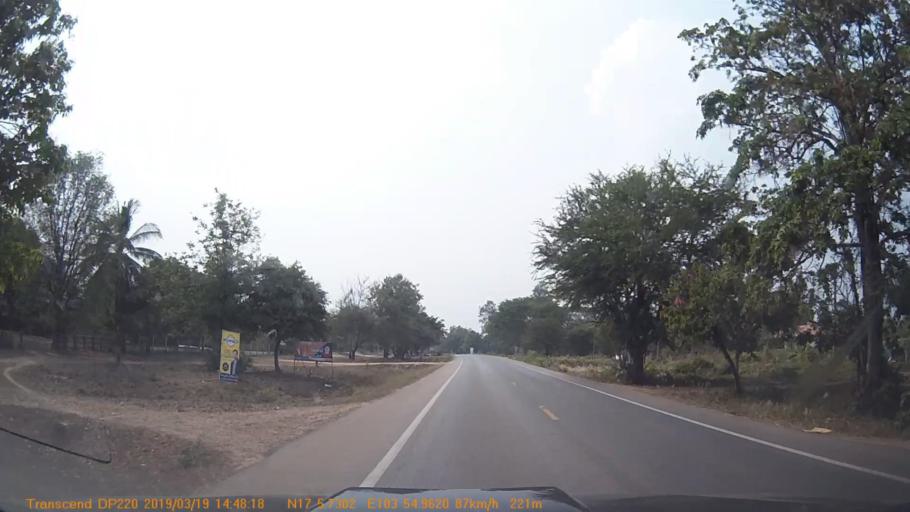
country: TH
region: Sakon Nakhon
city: Kut Bak
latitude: 17.0957
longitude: 103.9158
